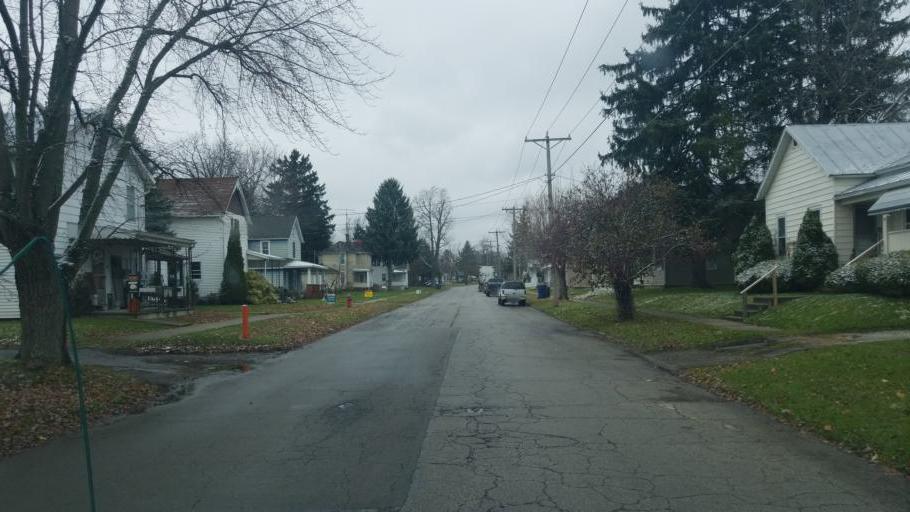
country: US
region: Ohio
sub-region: Richland County
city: Shelby
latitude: 40.8845
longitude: -82.6551
